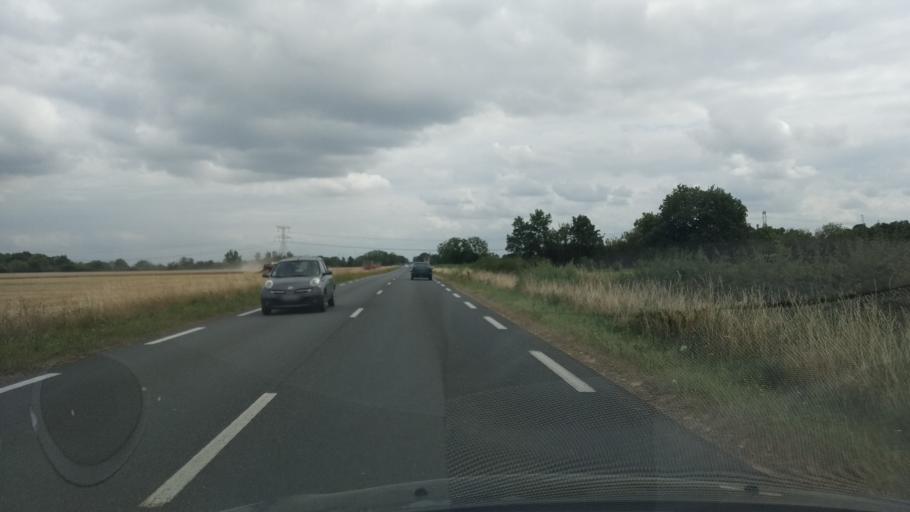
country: FR
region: Poitou-Charentes
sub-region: Departement de la Vienne
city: Saint-Maurice-la-Clouere
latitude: 46.4023
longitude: 0.3935
